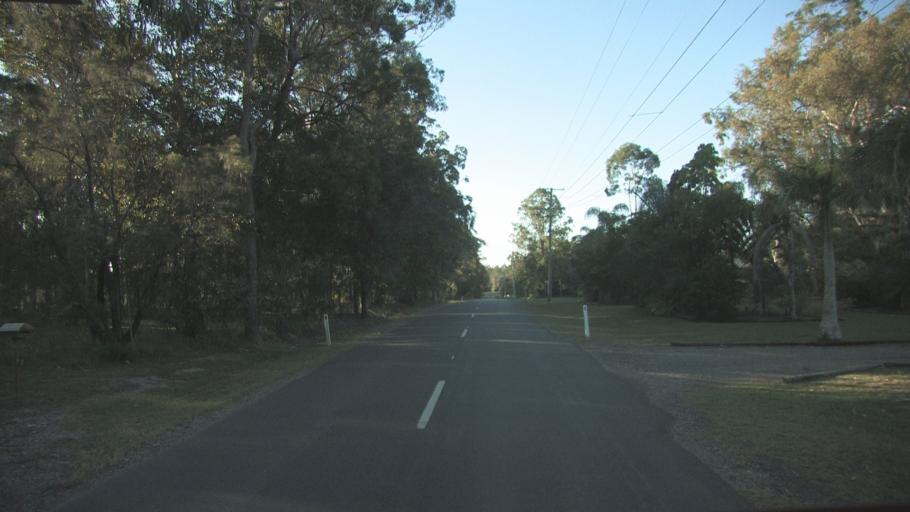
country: AU
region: Queensland
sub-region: Gold Coast
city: Yatala
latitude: -27.6795
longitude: 153.2753
